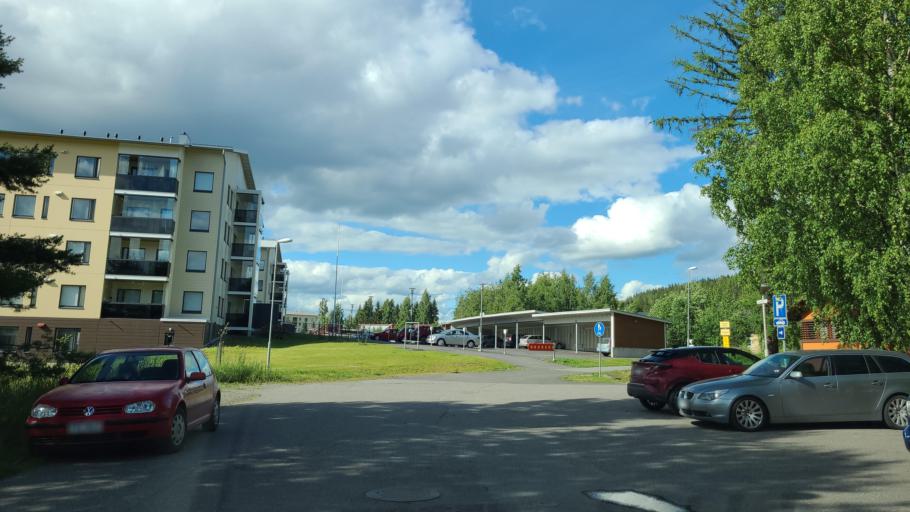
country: FI
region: Northern Savo
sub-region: Kuopio
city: Kuopio
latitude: 62.9270
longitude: 27.6304
